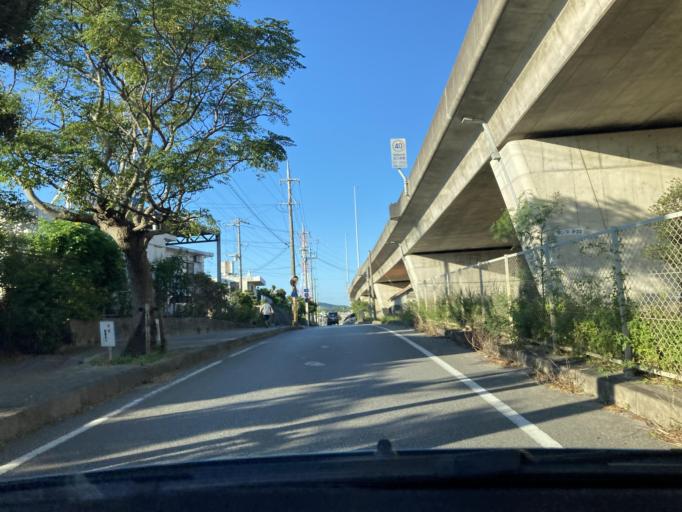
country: JP
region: Okinawa
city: Tomigusuku
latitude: 26.1936
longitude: 127.7393
